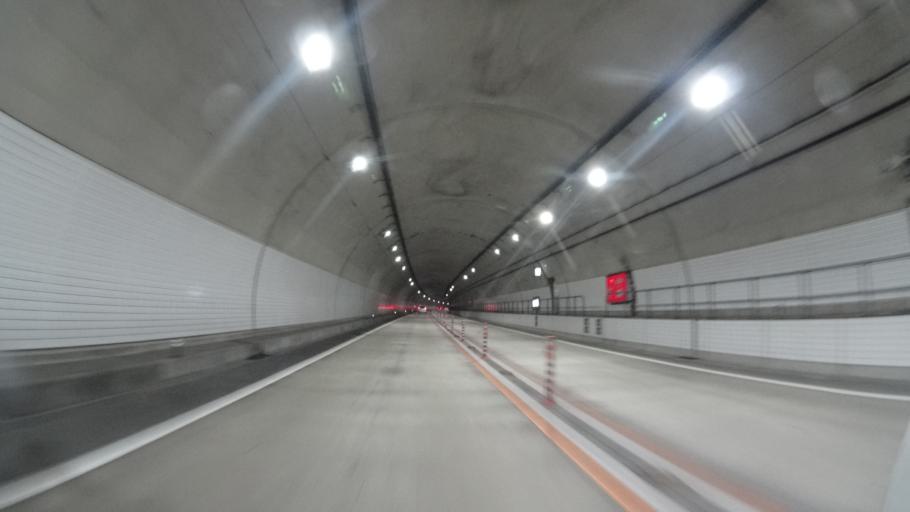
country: JP
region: Kyoto
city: Miyazu
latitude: 35.5536
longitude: 135.1316
